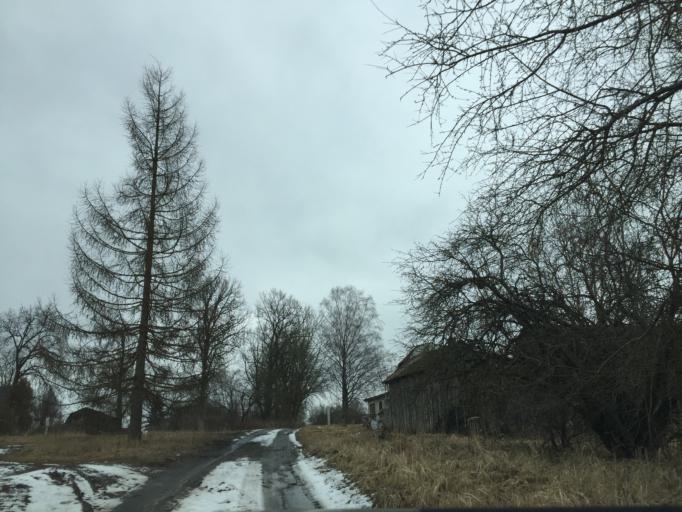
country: LV
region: Lielvarde
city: Lielvarde
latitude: 56.7530
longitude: 24.7801
